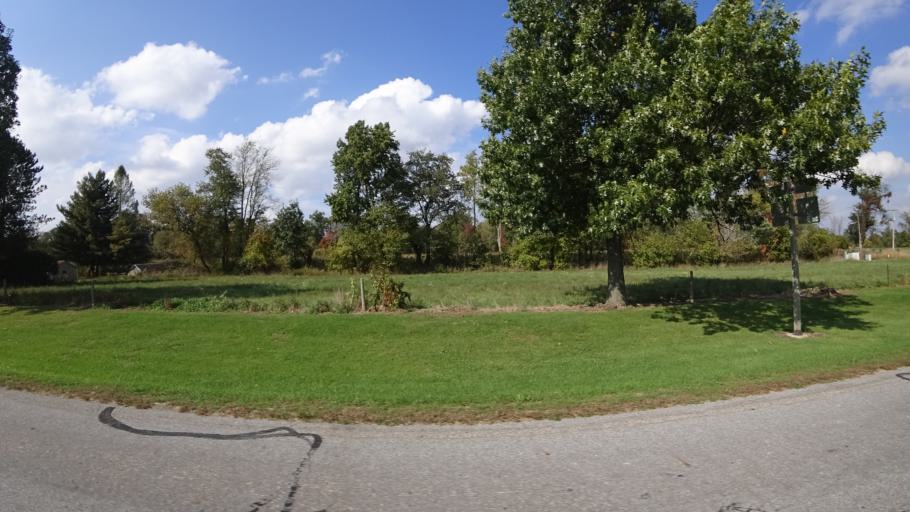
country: US
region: Michigan
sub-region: Saint Joseph County
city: Colon
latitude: 42.0338
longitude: -85.3326
